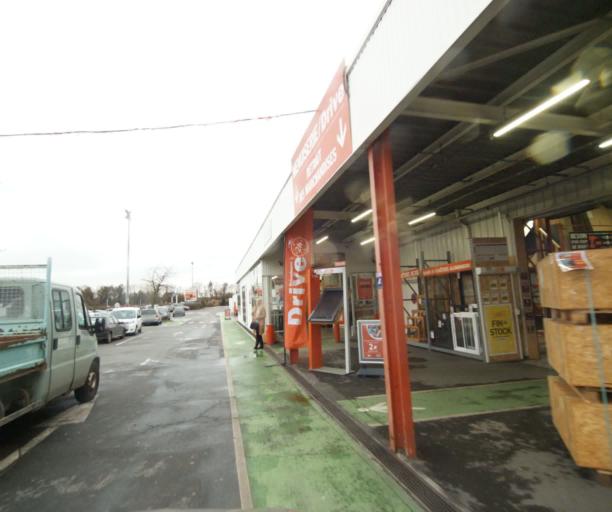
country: FR
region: Nord-Pas-de-Calais
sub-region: Departement du Nord
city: Petite-Foret
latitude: 50.3748
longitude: 3.4804
